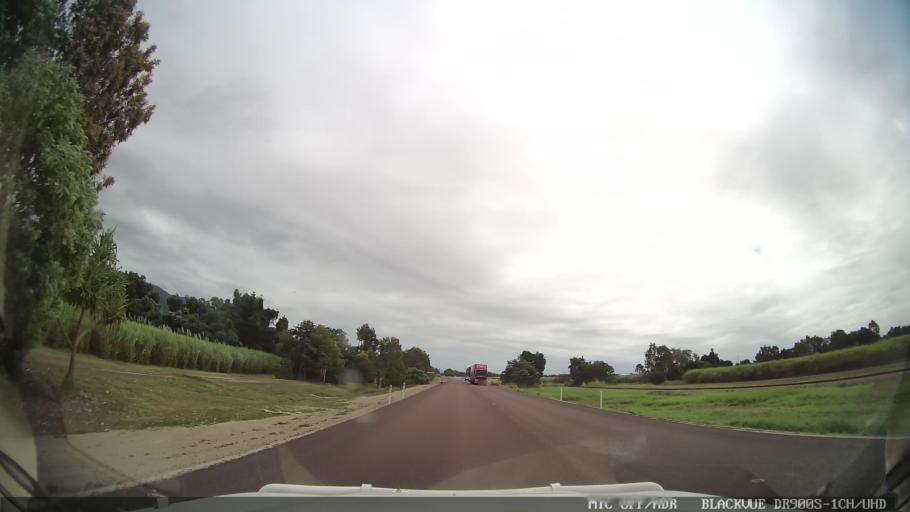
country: AU
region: Queensland
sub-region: Hinchinbrook
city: Ingham
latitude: -18.9243
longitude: 146.2616
